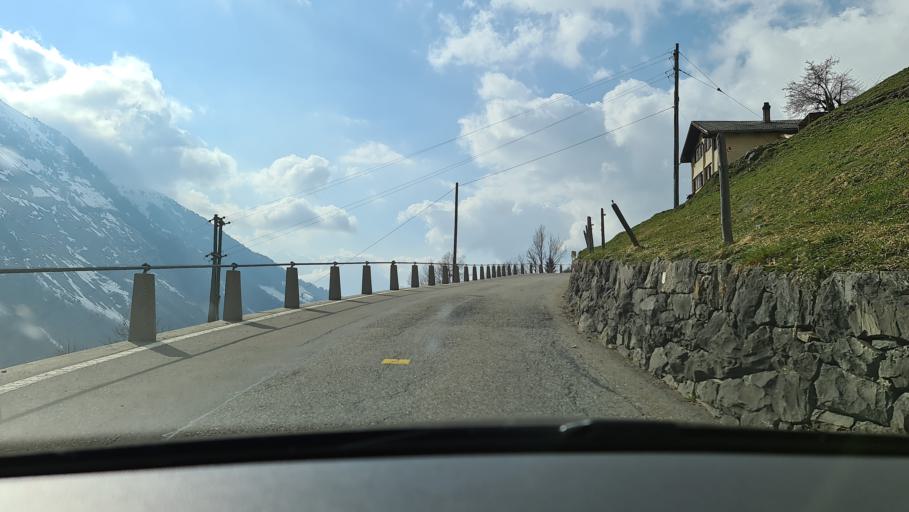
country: CH
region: Uri
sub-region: Uri
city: Burglen
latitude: 46.8673
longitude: 8.7703
